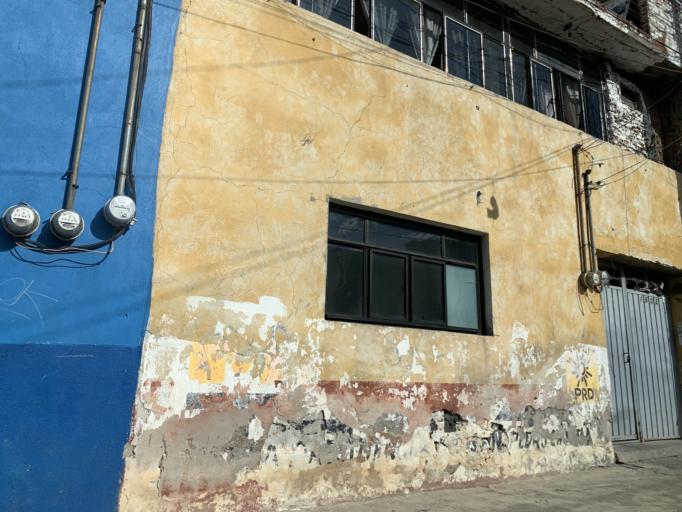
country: MX
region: Puebla
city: Cholula
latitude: 19.0700
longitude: -98.3065
